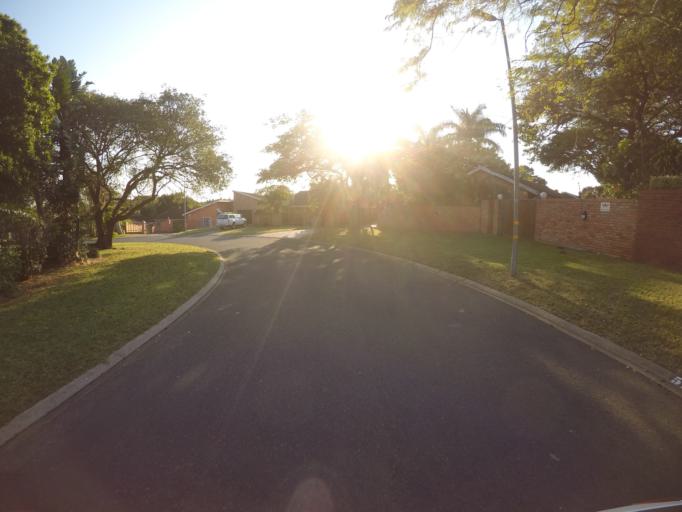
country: ZA
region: KwaZulu-Natal
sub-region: uThungulu District Municipality
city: Richards Bay
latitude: -28.7724
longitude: 32.1170
